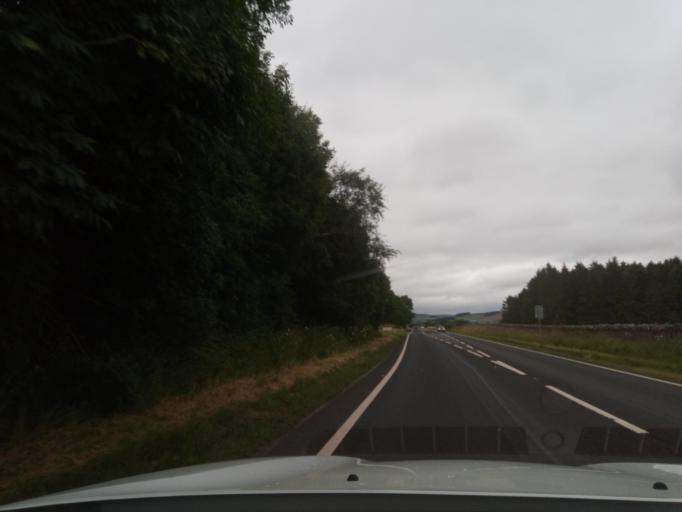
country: GB
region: Scotland
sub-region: The Scottish Borders
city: Lauder
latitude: 55.7342
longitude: -2.7652
